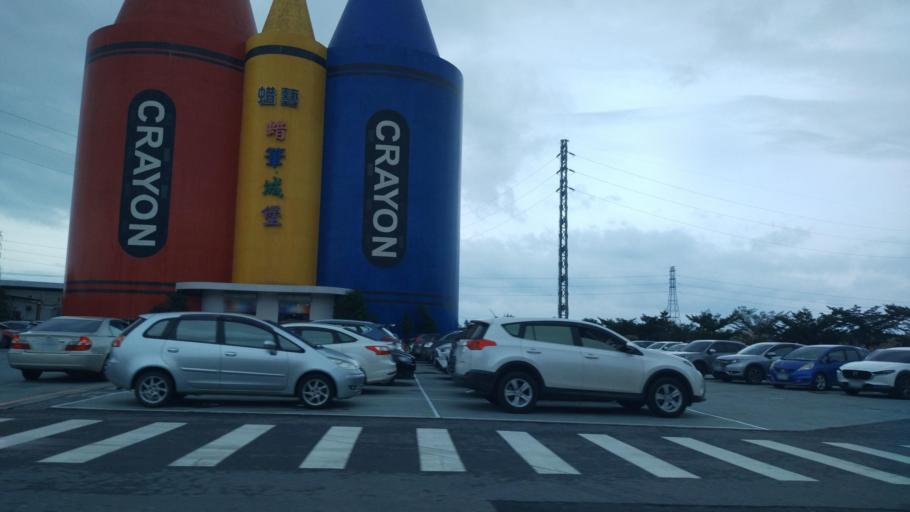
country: TW
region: Taiwan
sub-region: Yilan
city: Yilan
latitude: 24.6159
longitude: 121.8279
